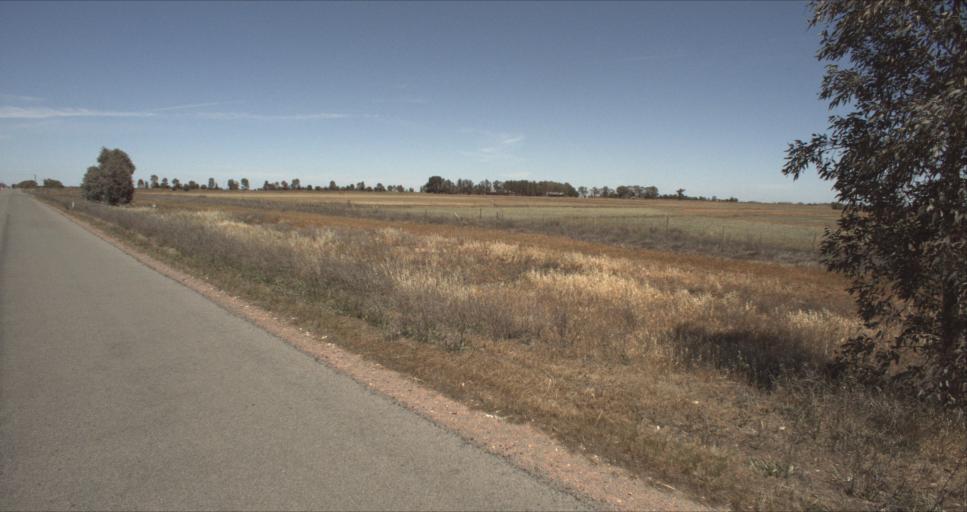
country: AU
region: New South Wales
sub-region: Leeton
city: Leeton
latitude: -34.4362
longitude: 146.2987
